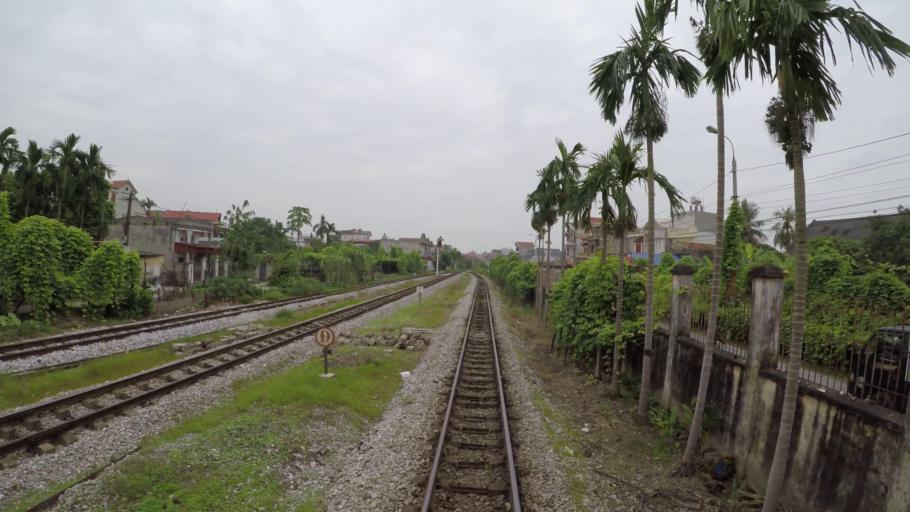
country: VN
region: Hai Duong
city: Phu Thai
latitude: 20.9699
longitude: 106.4978
